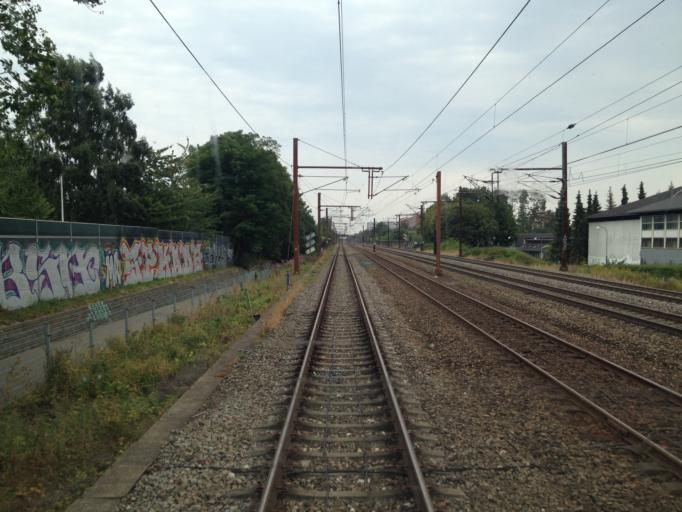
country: DK
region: Capital Region
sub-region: Brondby Kommune
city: Brondbyvester
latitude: 55.6652
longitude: 12.4290
